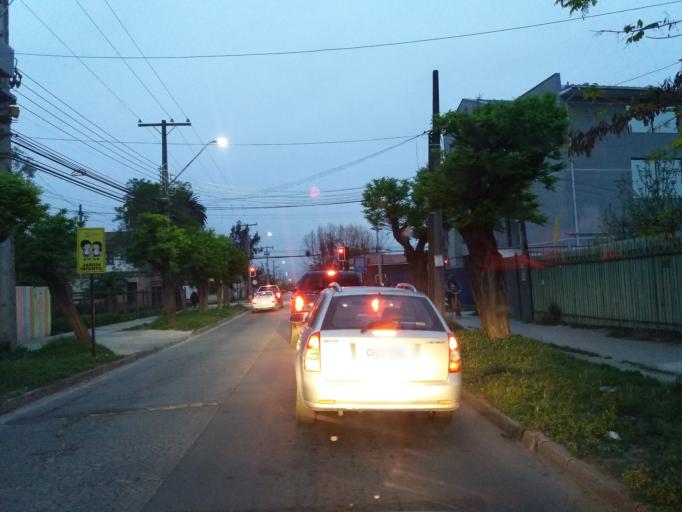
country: CL
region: Valparaiso
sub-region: Provincia de Marga Marga
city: Limache
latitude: -33.0042
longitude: -71.2670
